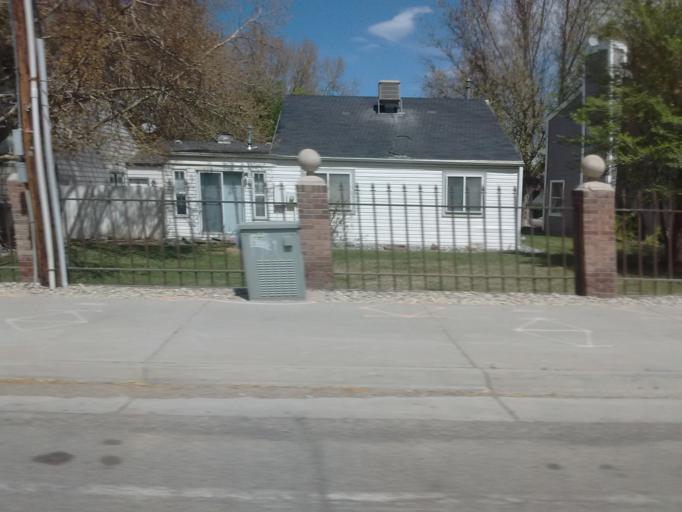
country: US
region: Colorado
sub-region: Mesa County
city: Redlands
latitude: 39.0826
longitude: -108.6423
